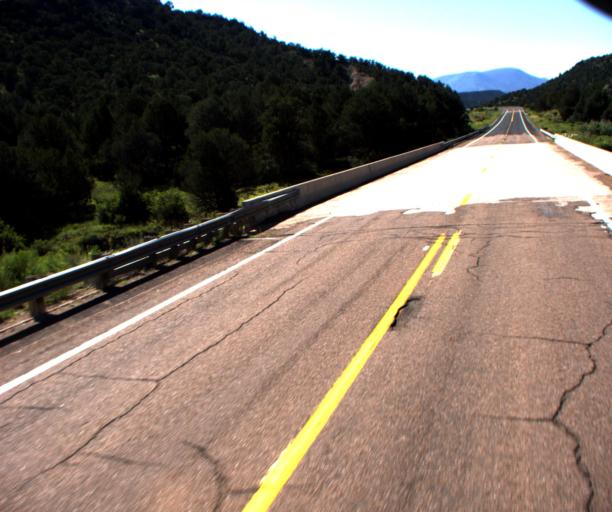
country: US
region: Arizona
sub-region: Apache County
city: Eagar
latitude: 34.0661
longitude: -109.1996
